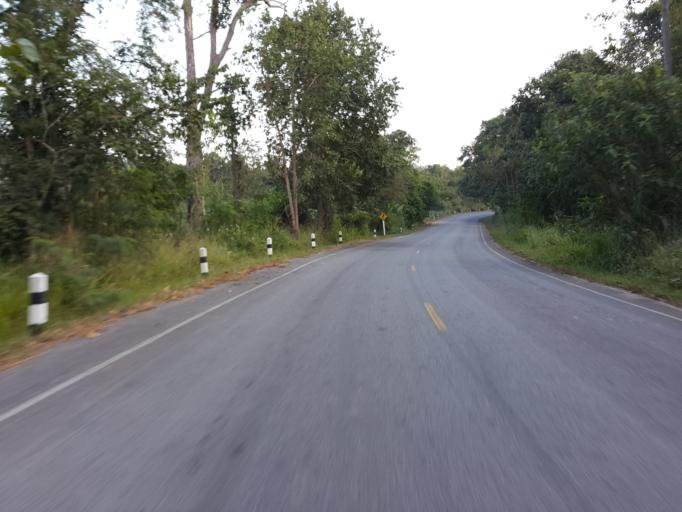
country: TH
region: Lamphun
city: Thung Hua Chang
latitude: 17.9232
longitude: 99.0545
